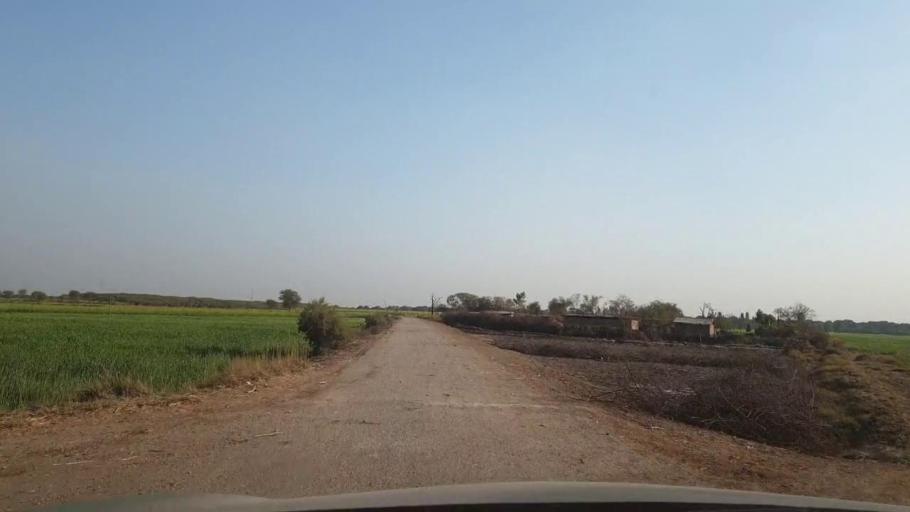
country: PK
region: Sindh
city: Tando Allahyar
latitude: 25.5879
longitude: 68.6702
